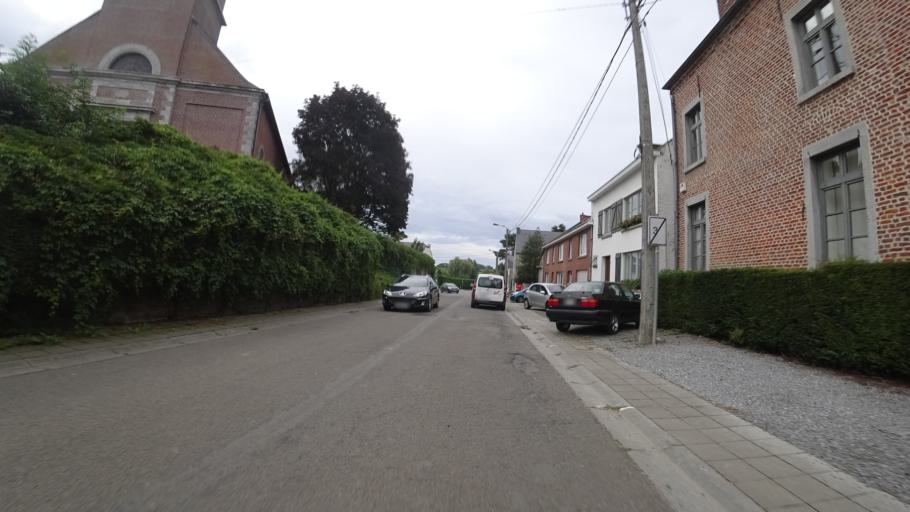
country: BE
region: Wallonia
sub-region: Province du Brabant Wallon
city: Perwez
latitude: 50.5816
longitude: 4.7658
